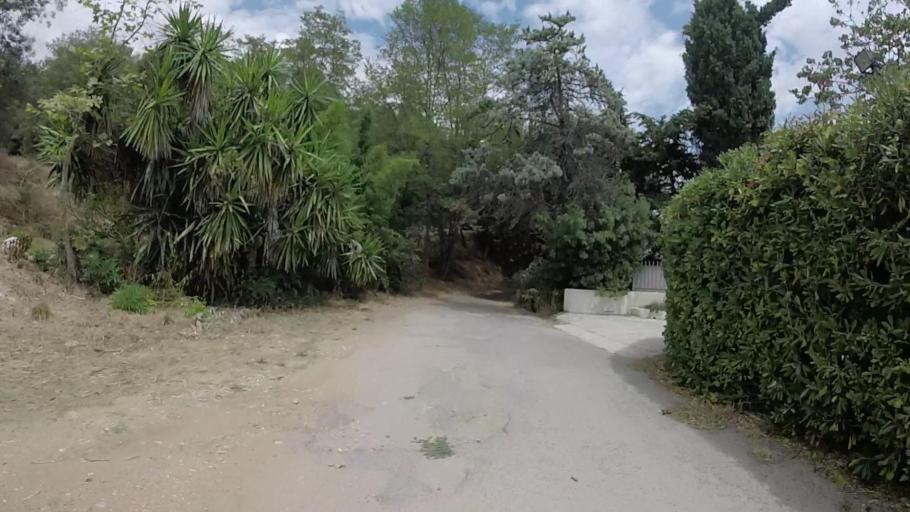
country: FR
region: Provence-Alpes-Cote d'Azur
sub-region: Departement des Alpes-Maritimes
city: Biot
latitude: 43.6197
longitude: 7.0984
